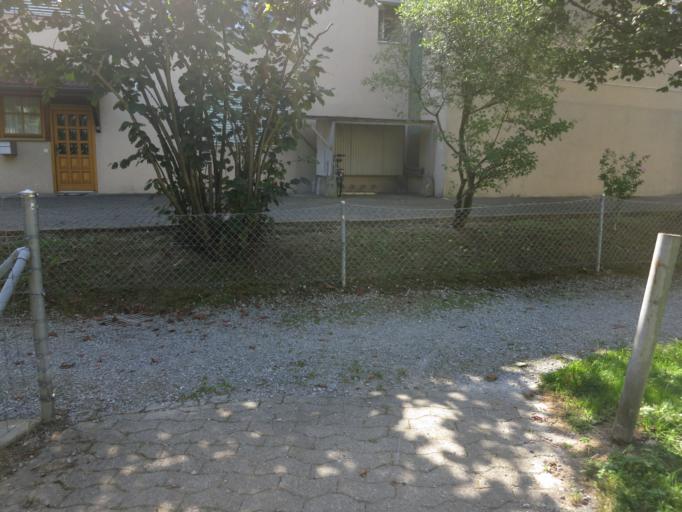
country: CH
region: Zurich
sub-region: Bezirk Meilen
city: Hombrechtikon
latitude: 47.2481
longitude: 8.7733
